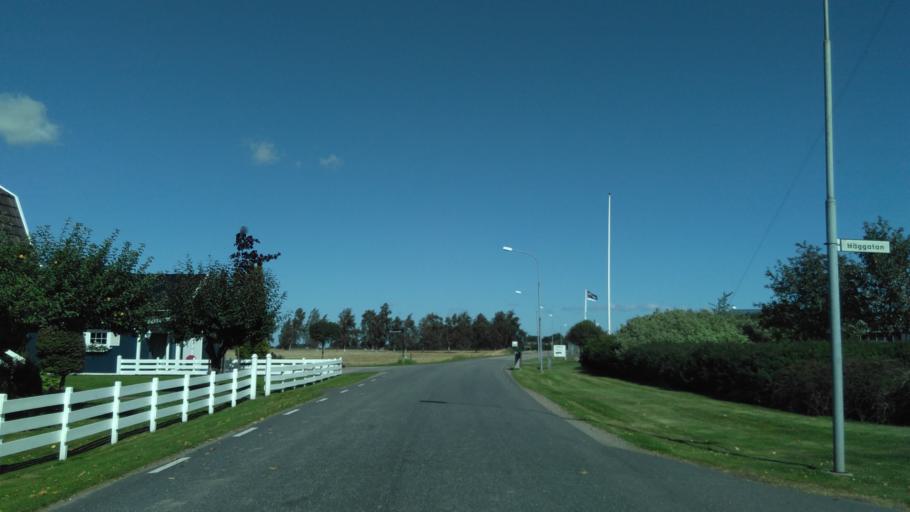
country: SE
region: Vaestra Goetaland
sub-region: Vara Kommun
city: Vara
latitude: 58.2563
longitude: 12.9985
